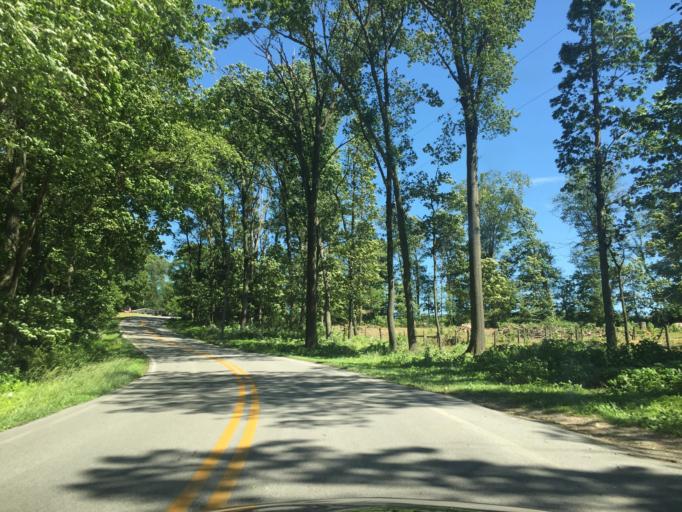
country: US
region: Maryland
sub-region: Carroll County
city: Manchester
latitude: 39.6343
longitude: -76.9165
